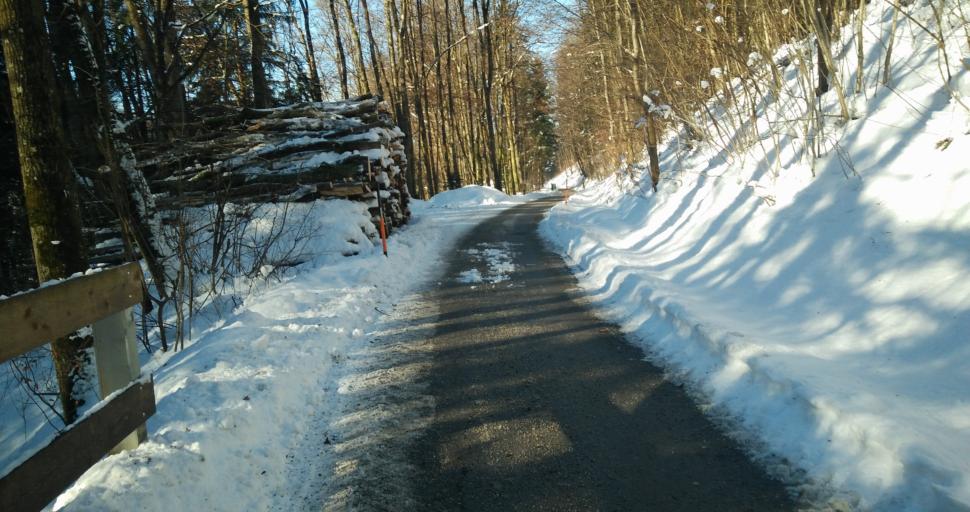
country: AT
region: Salzburg
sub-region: Politischer Bezirk Salzburg-Umgebung
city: Hallwang
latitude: 47.8437
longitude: 13.0922
